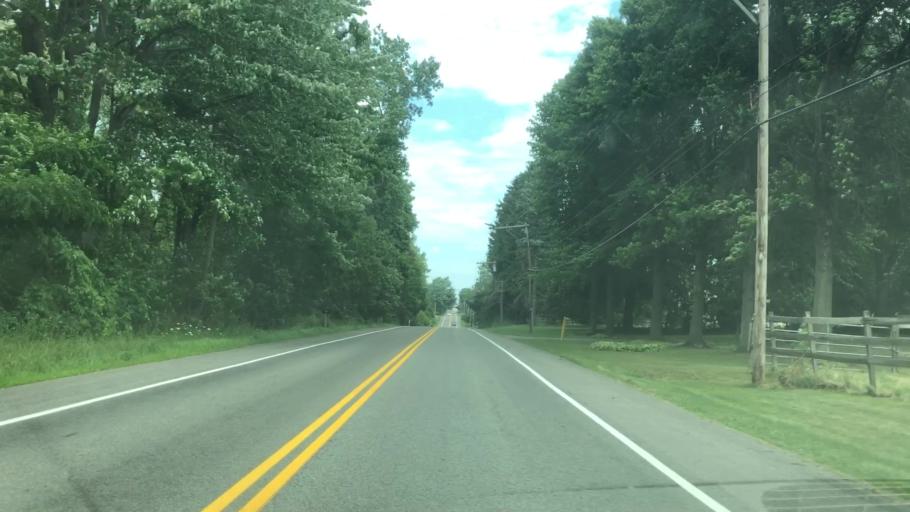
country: US
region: New York
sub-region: Monroe County
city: Fairport
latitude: 43.1324
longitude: -77.4005
